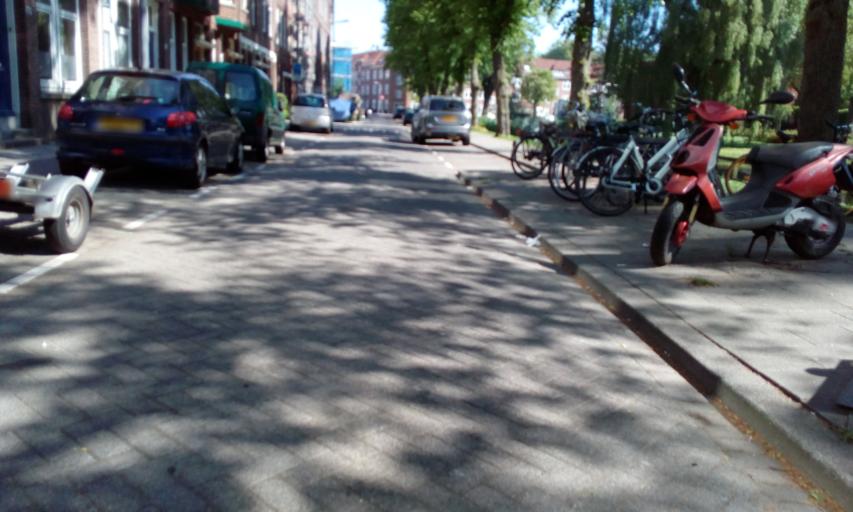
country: NL
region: South Holland
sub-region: Gemeente Rotterdam
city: Rotterdam
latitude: 51.9347
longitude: 4.4927
